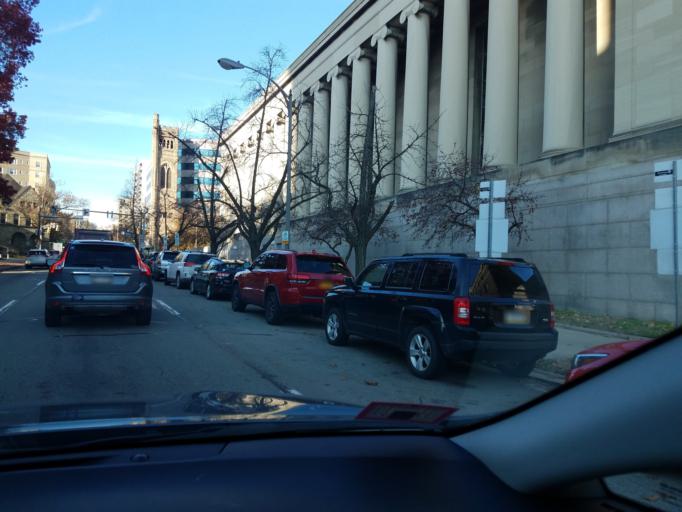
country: US
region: Pennsylvania
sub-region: Allegheny County
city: Bloomfield
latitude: 40.4456
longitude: -79.9515
